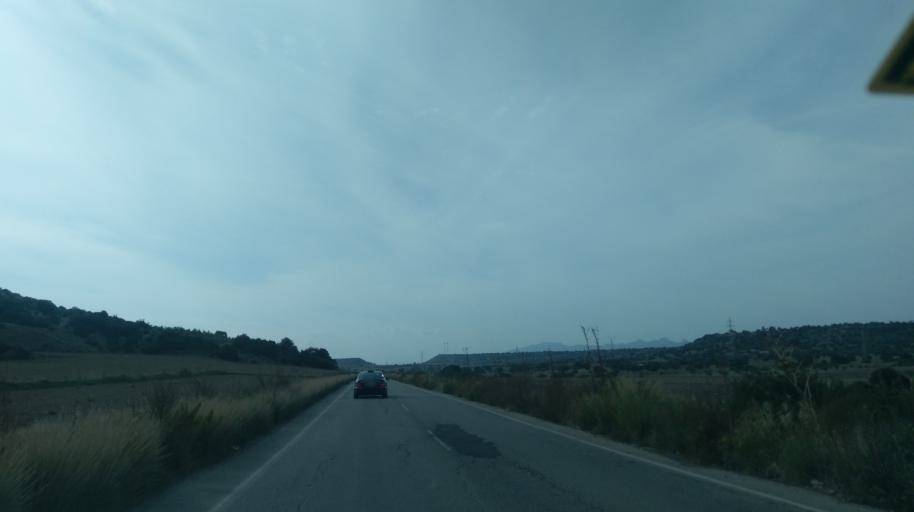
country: CY
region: Ammochostos
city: Leonarisso
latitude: 35.4008
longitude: 34.0767
